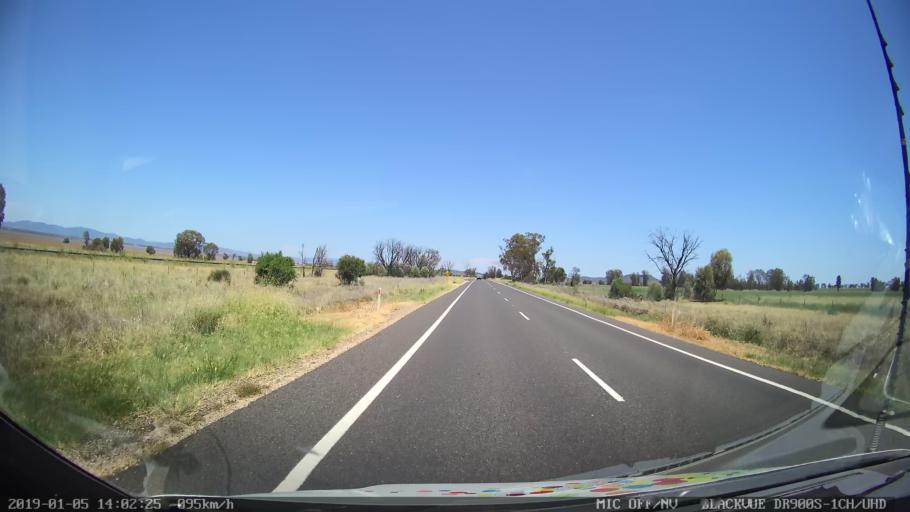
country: AU
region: New South Wales
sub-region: Gunnedah
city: Gunnedah
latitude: -31.1795
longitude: 150.3376
